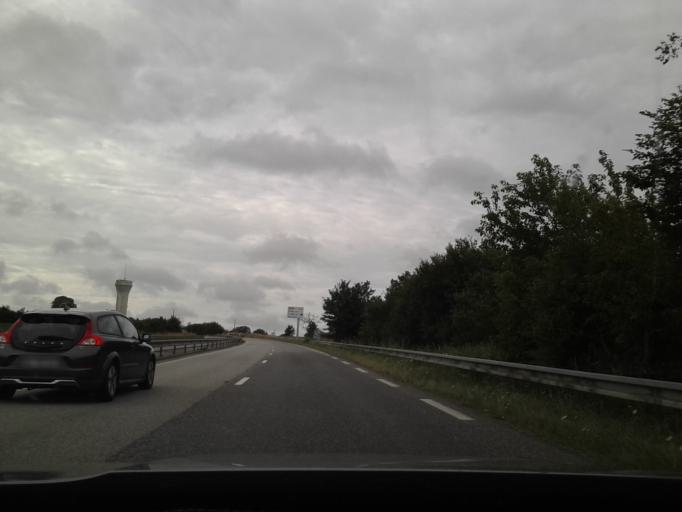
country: FR
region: Lower Normandy
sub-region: Departement de la Manche
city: Carentan
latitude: 49.3457
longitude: -1.2750
